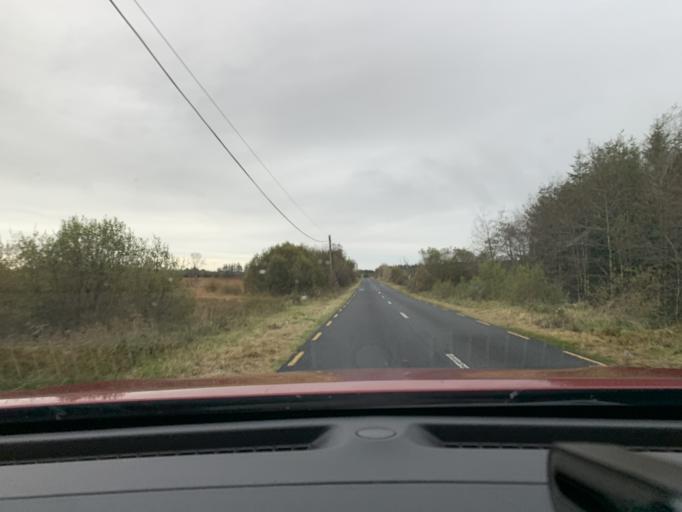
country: IE
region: Connaught
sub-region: Roscommon
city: Ballaghaderreen
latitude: 53.9487
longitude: -8.5454
